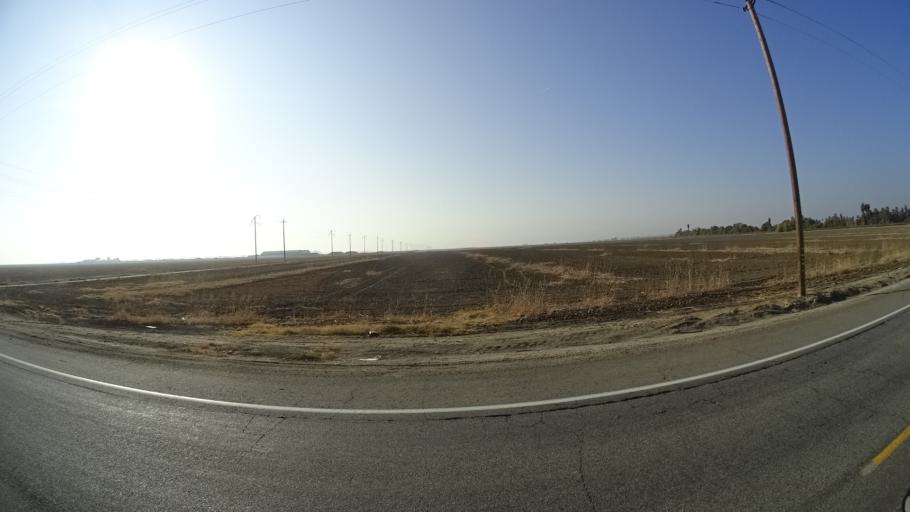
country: US
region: California
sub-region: Kern County
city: Greenfield
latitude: 35.2376
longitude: -118.9774
